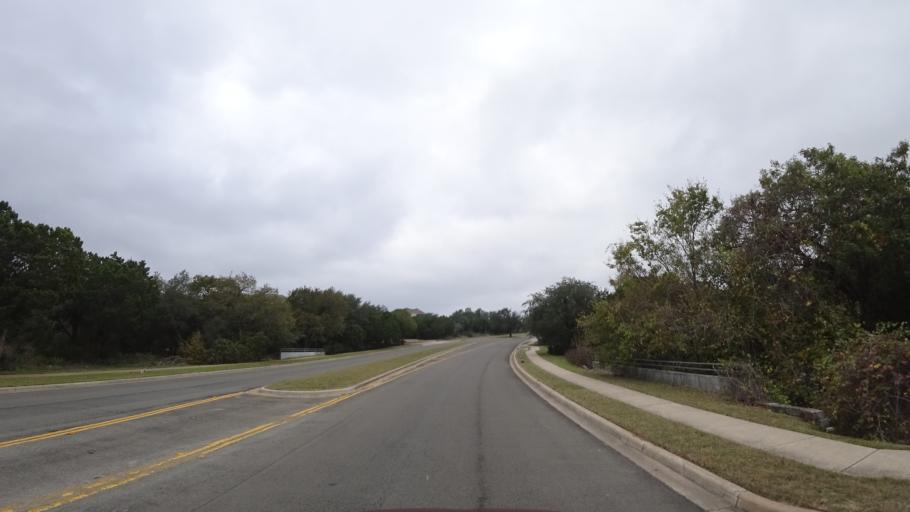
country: US
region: Texas
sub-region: Williamson County
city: Anderson Mill
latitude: 30.4285
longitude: -97.8396
